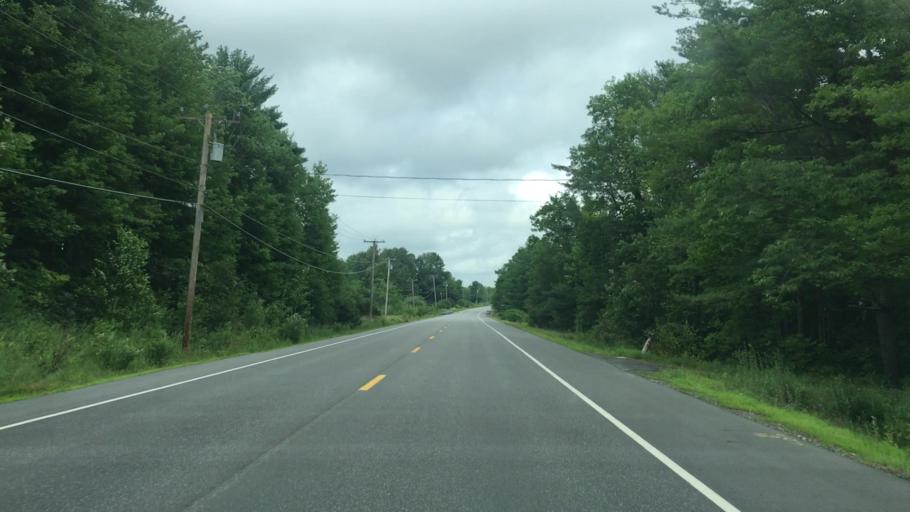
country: US
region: Maine
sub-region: Kennebec County
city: Pittston
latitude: 44.2076
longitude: -69.7544
